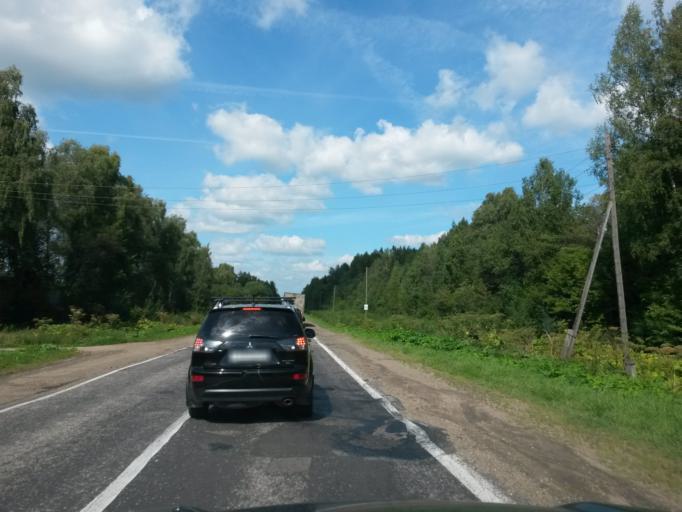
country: RU
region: Jaroslavl
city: Yaroslavl
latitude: 57.4960
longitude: 39.9003
